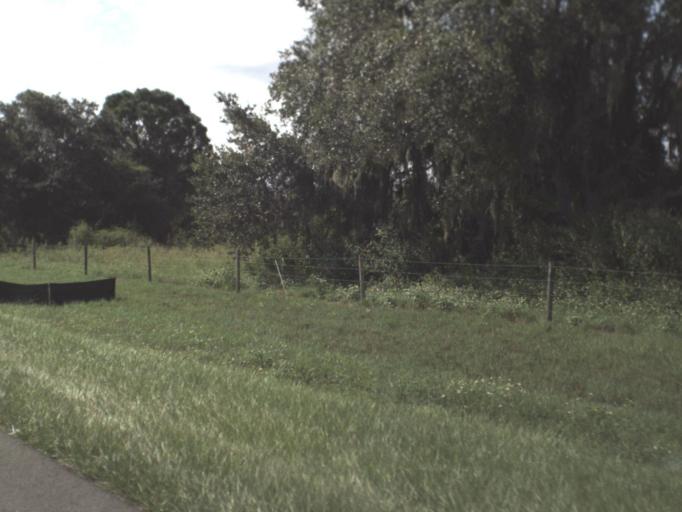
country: US
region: Florida
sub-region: Sarasota County
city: The Meadows
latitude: 27.4747
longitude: -82.3168
